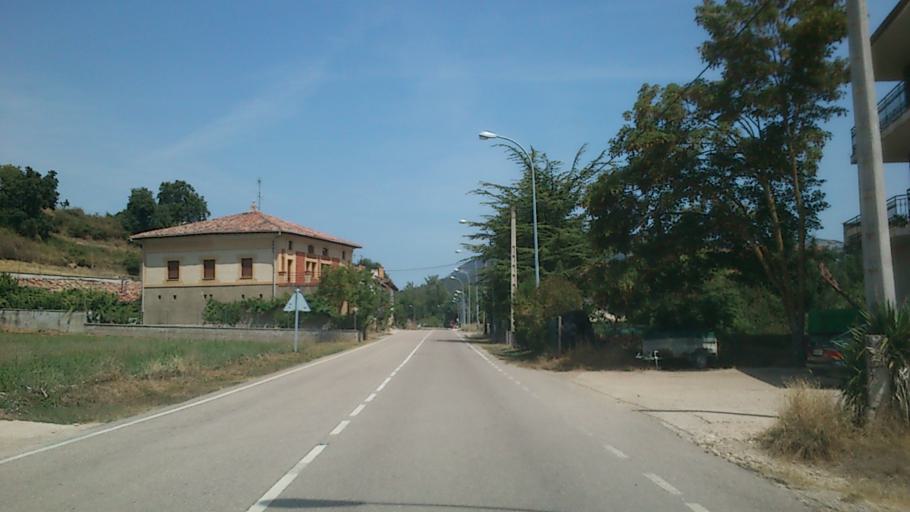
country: ES
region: Castille and Leon
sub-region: Provincia de Burgos
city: Trespaderne
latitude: 42.8523
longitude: -3.3336
